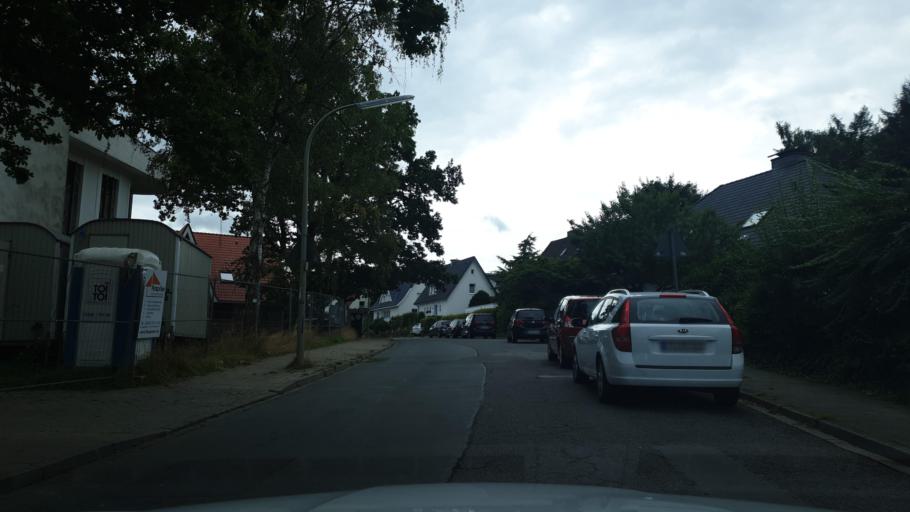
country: DE
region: Lower Saxony
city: Osnabrueck
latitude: 52.2517
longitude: 8.0429
